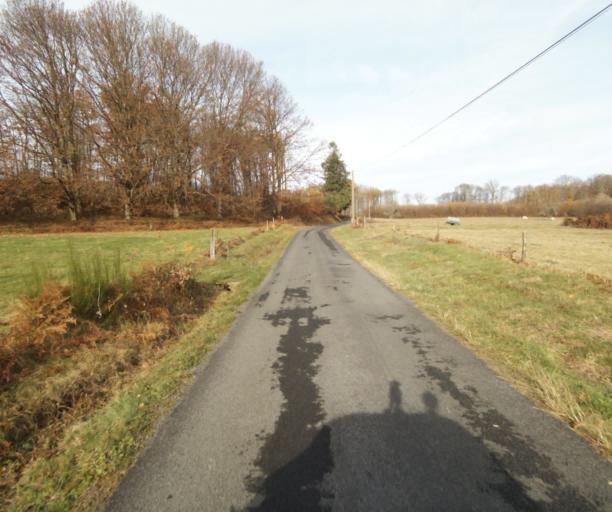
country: FR
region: Limousin
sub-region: Departement de la Correze
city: Sainte-Fortunade
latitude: 45.1703
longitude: 1.7460
